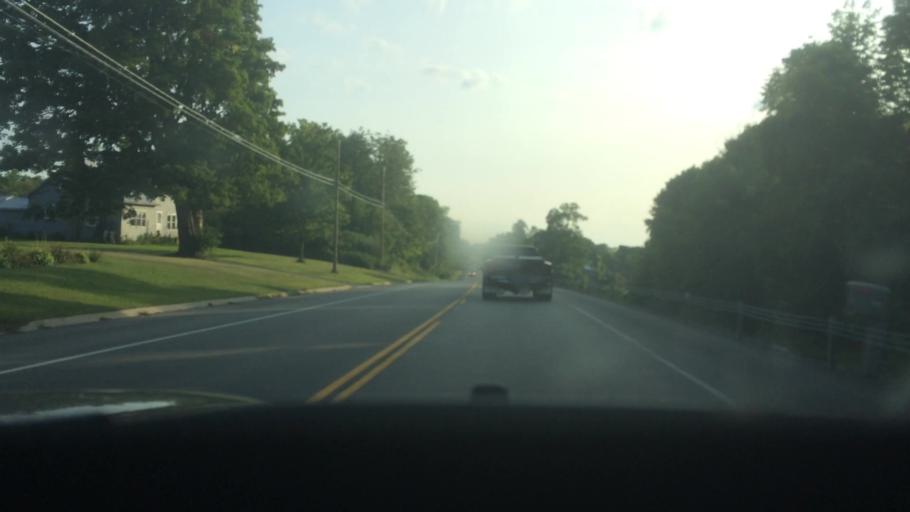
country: CA
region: Ontario
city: Prescott
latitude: 44.6754
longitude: -75.5254
